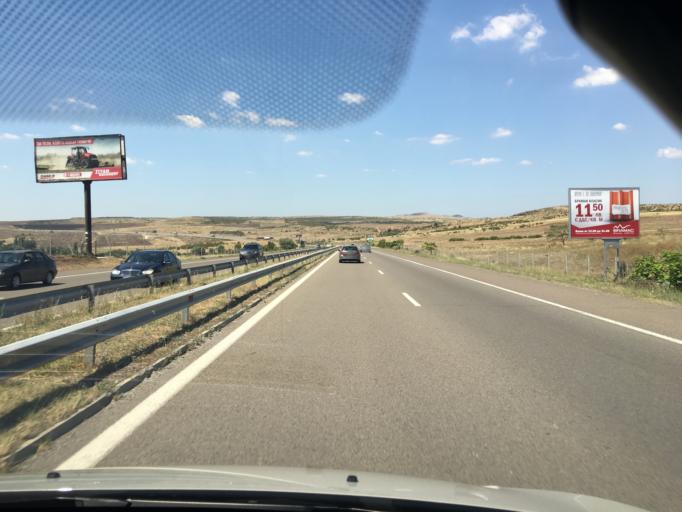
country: BG
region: Burgas
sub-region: Obshtina Kameno
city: Kameno
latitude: 42.5915
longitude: 27.1771
